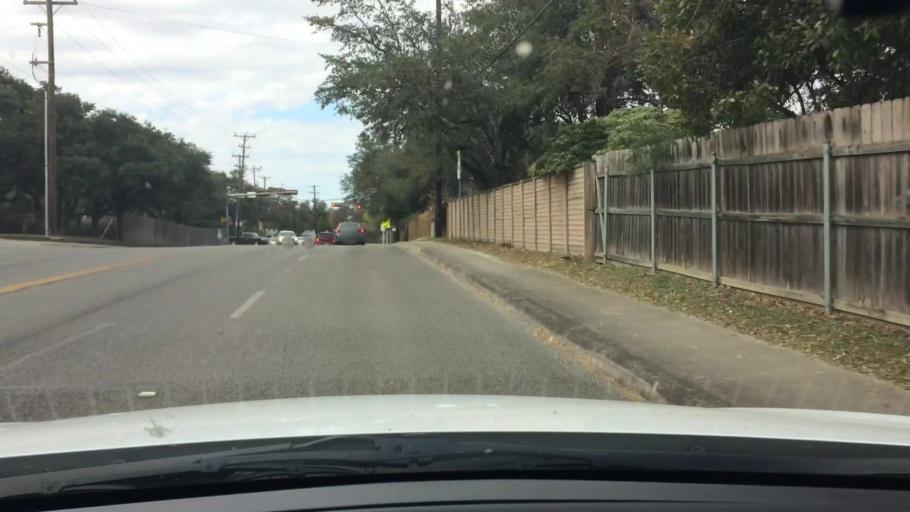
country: US
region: Texas
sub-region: Bexar County
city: Hollywood Park
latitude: 29.5751
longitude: -98.4668
